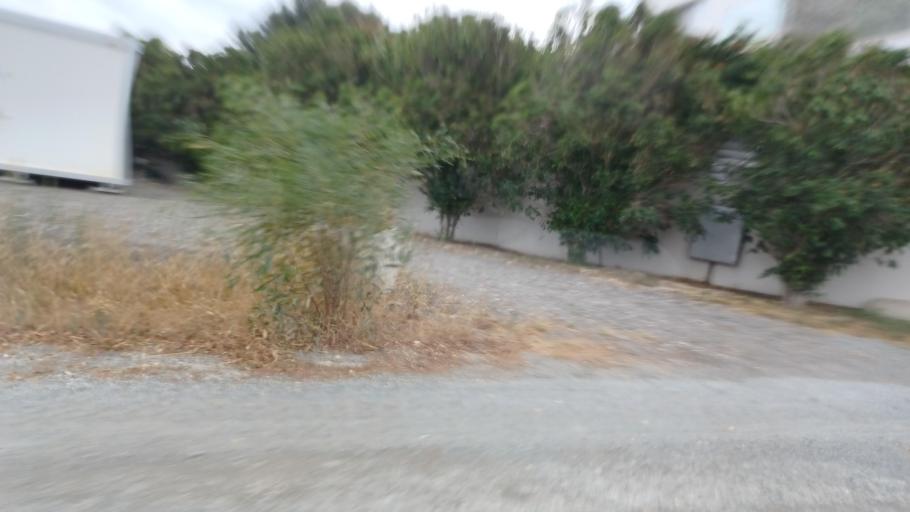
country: CY
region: Ammochostos
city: Protaras
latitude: 35.0197
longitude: 34.0277
